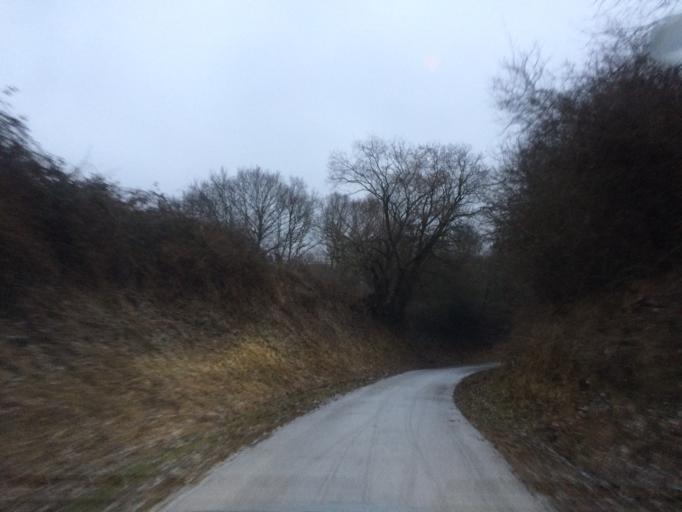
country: DE
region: Hesse
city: Trendelburg
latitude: 51.5780
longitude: 9.4049
